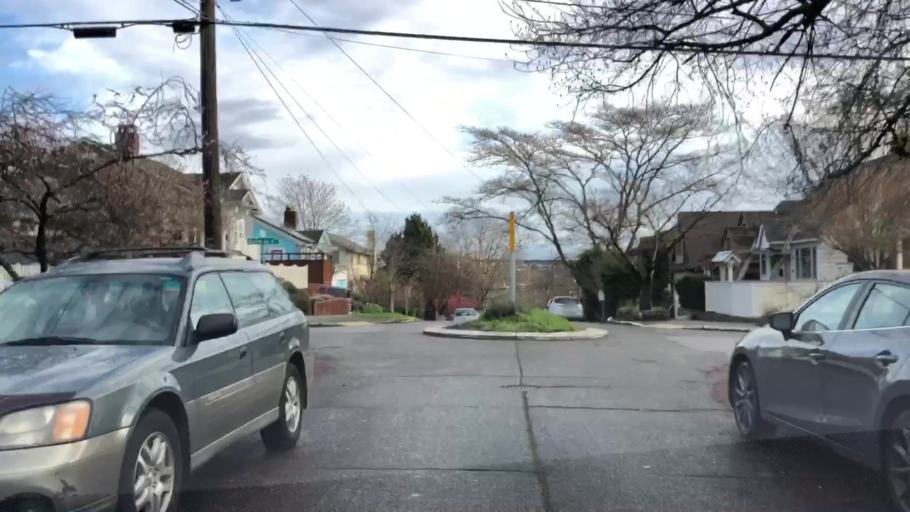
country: US
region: Washington
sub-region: King County
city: Seattle
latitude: 47.6492
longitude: -122.3355
